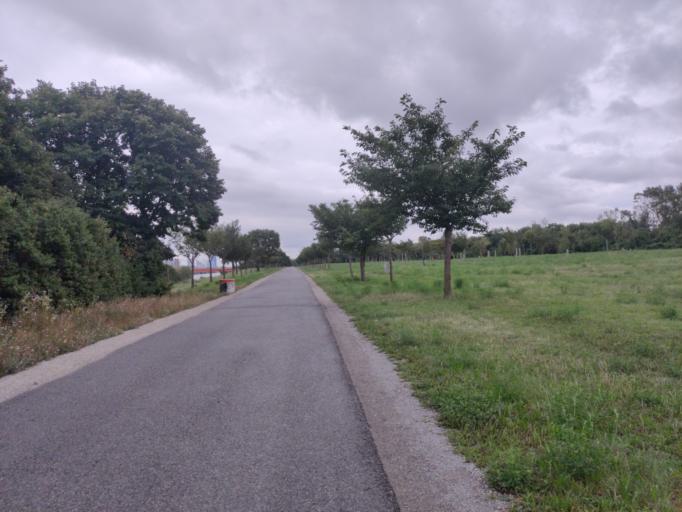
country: AT
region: Lower Austria
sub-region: Politischer Bezirk Korneuburg
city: Langenzersdorf
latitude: 48.2711
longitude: 16.3683
